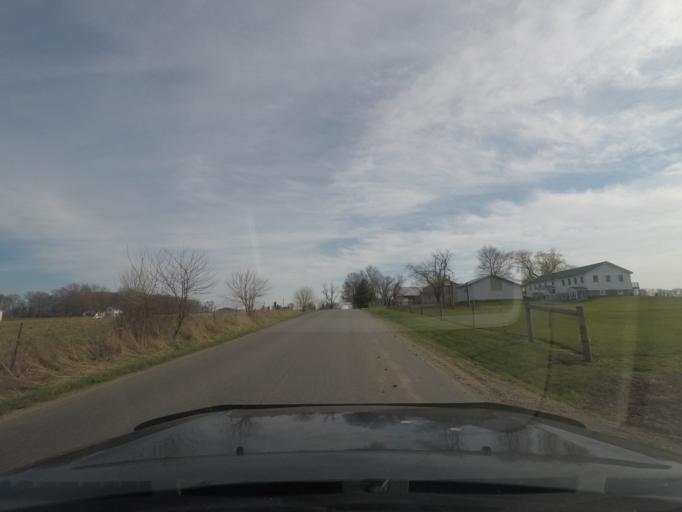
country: US
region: Indiana
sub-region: Elkhart County
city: Dunlap
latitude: 41.5478
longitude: -85.9248
